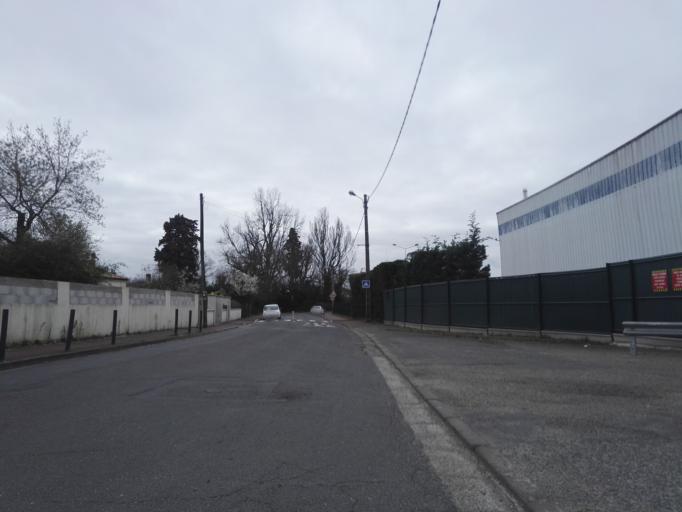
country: FR
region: Aquitaine
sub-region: Departement de la Gironde
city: Talence
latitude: 44.8010
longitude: -0.5812
